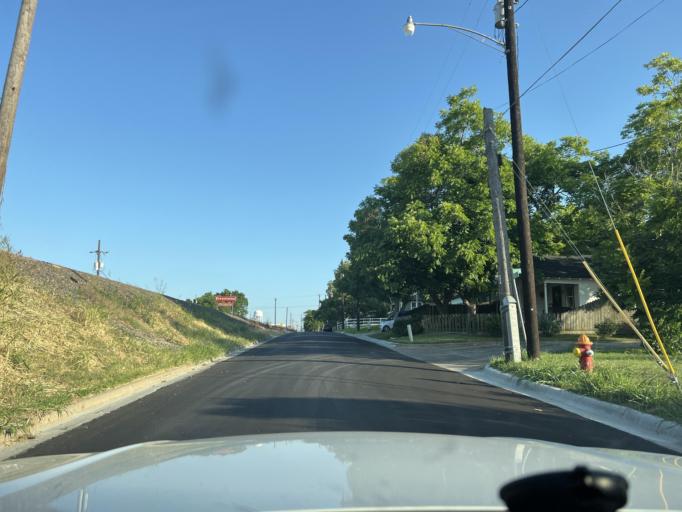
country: US
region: Texas
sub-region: Washington County
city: Brenham
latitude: 30.1691
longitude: -96.4009
